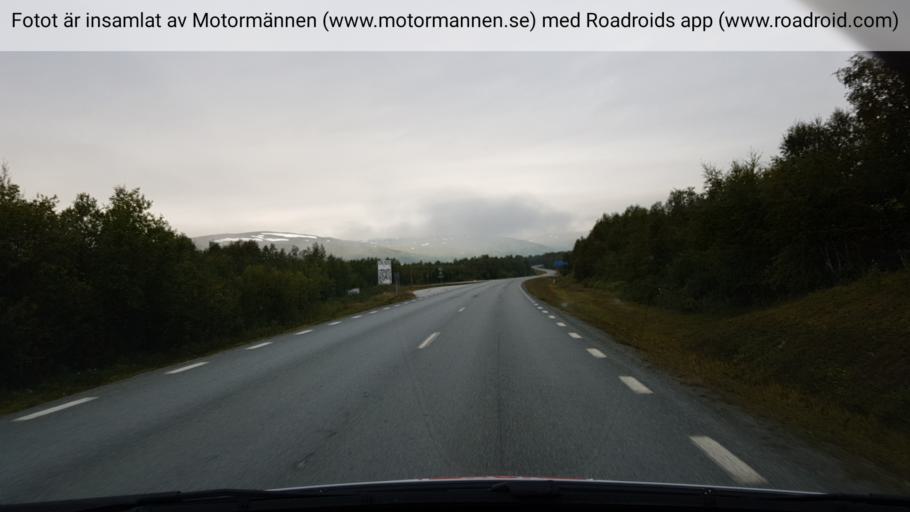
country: NO
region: Nordland
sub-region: Rana
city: Mo i Rana
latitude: 65.8336
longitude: 15.0561
